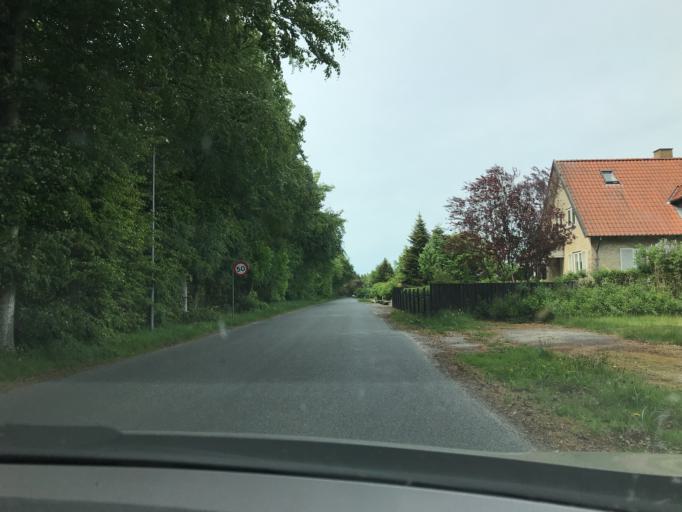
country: DK
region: Central Jutland
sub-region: Norddjurs Kommune
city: Allingabro
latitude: 56.6003
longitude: 10.3106
